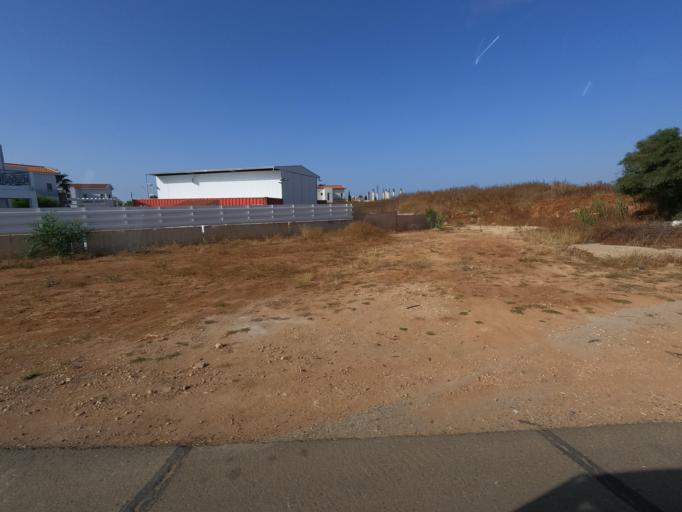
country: CY
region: Ammochostos
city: Liopetri
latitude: 34.9824
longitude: 33.9307
